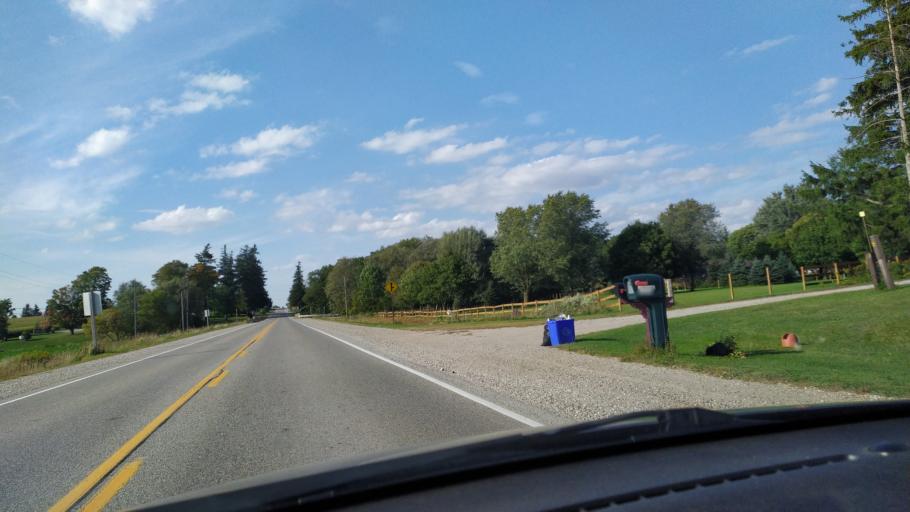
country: CA
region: Ontario
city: Ingersoll
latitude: 43.1609
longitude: -80.9036
